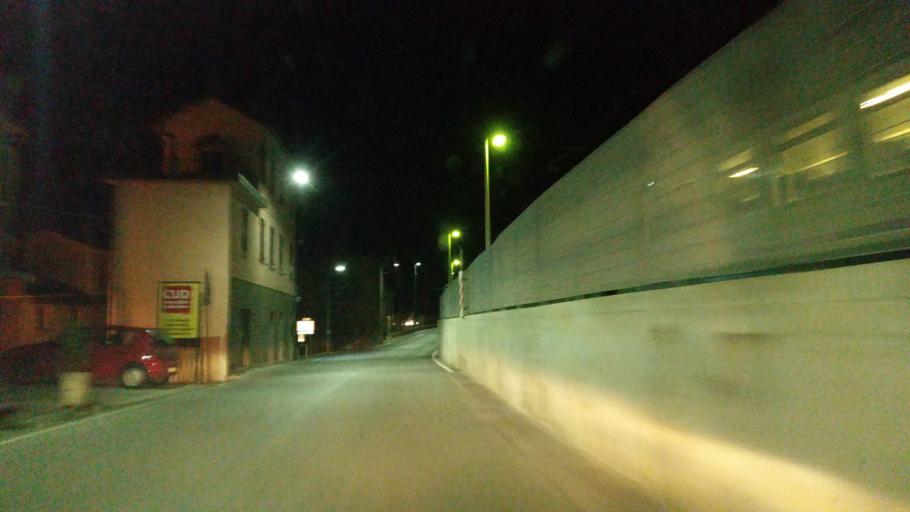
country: IT
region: Liguria
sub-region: Provincia di Savona
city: Bormida-Genepro
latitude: 44.3906
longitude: 8.1914
